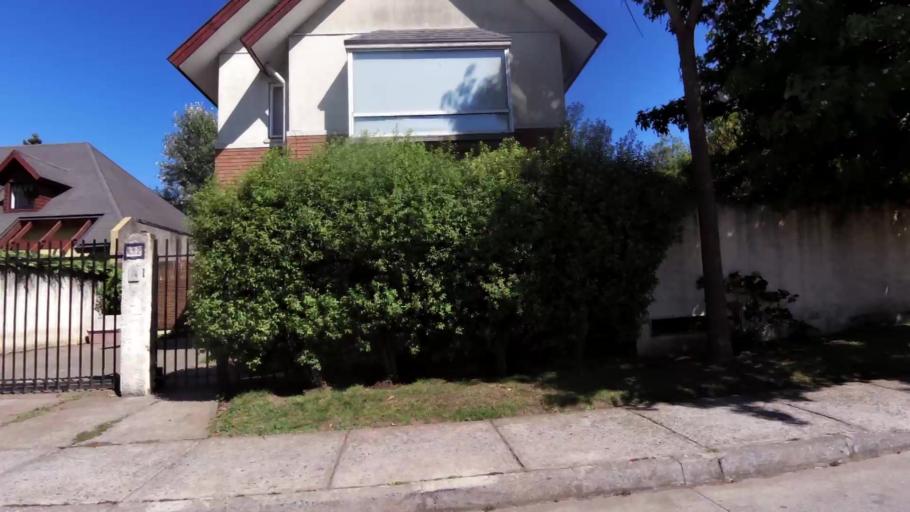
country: CL
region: Biobio
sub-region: Provincia de Concepcion
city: Concepcion
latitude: -36.7902
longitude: -73.0543
